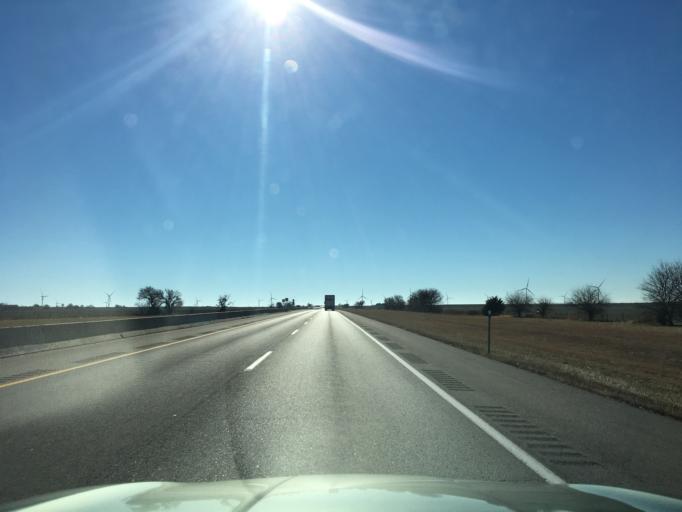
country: US
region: Kansas
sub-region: Sumner County
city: Wellington
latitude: 37.1798
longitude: -97.3396
